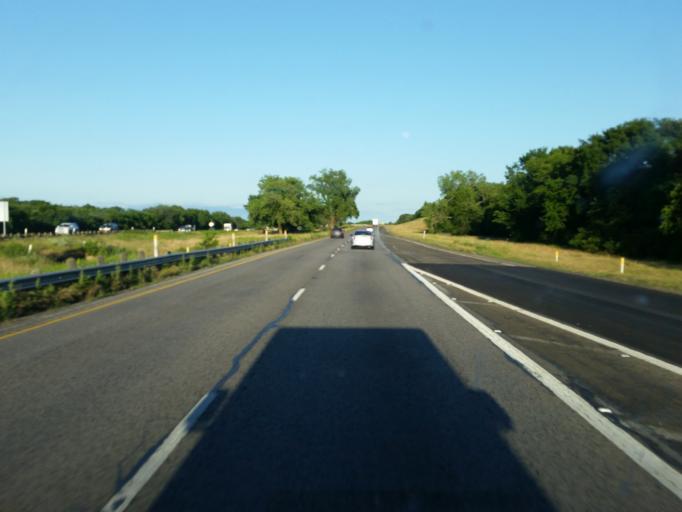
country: US
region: Texas
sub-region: Kaufman County
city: Terrell
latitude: 32.6800
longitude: -96.1918
